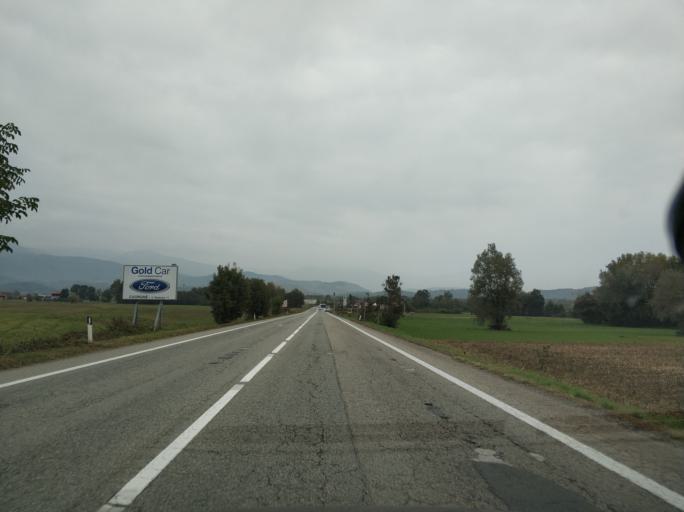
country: IT
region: Piedmont
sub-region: Provincia di Torino
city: Castellamonte
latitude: 45.3769
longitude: 7.7320
